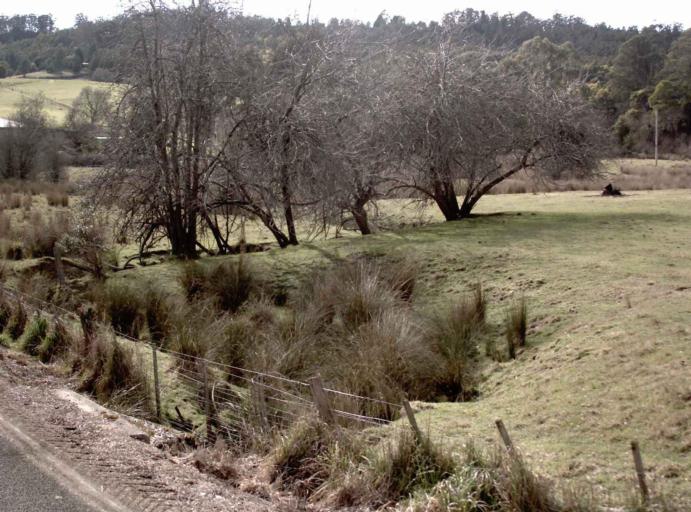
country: AU
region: Tasmania
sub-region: Launceston
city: Mayfield
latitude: -41.2499
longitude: 147.2457
